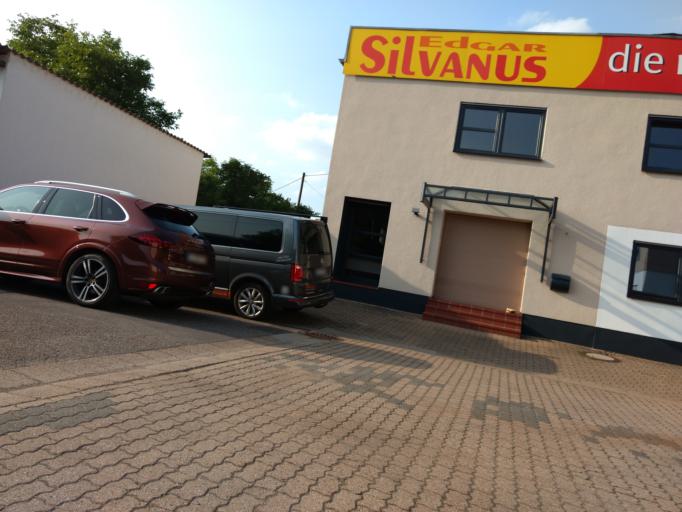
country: DE
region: Saarland
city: Rehlingen-Siersburg
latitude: 49.3540
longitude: 6.6734
